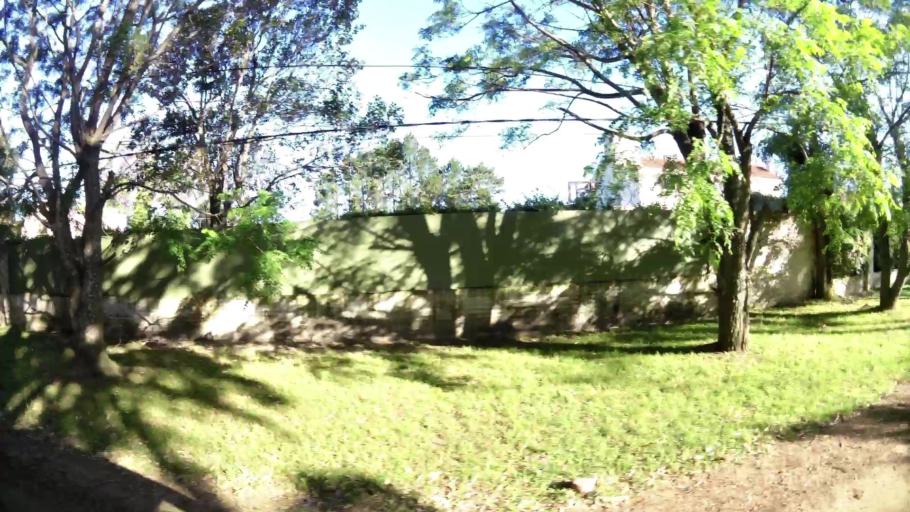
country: UY
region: Canelones
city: Paso de Carrasco
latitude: -34.8576
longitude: -56.0375
